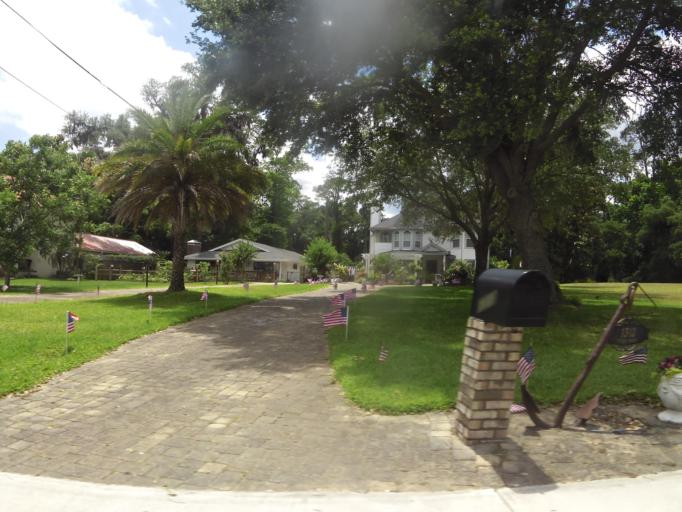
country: US
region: Florida
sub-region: Clay County
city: Orange Park
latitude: 30.1741
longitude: -81.6975
